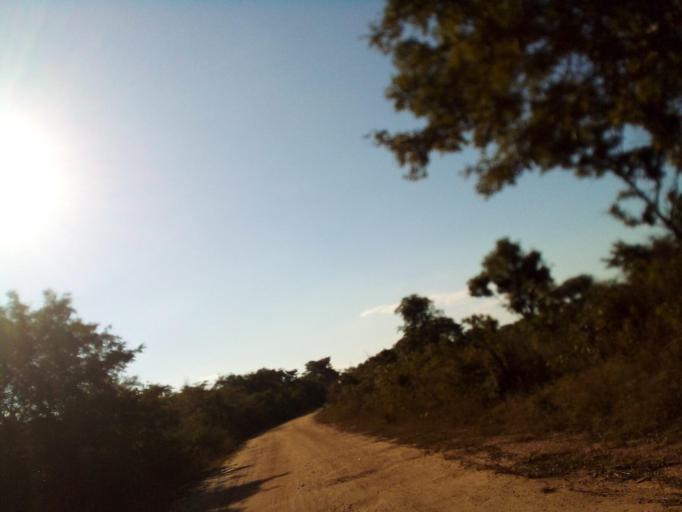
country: MZ
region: Zambezia
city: Quelimane
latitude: -17.4805
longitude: 36.5429
